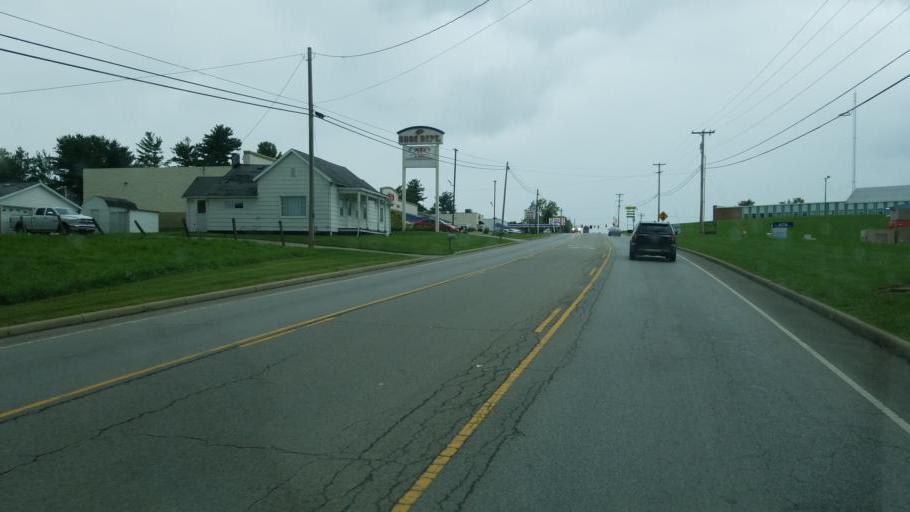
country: US
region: Ohio
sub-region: Jackson County
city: Jackson
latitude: 39.0307
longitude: -82.6239
